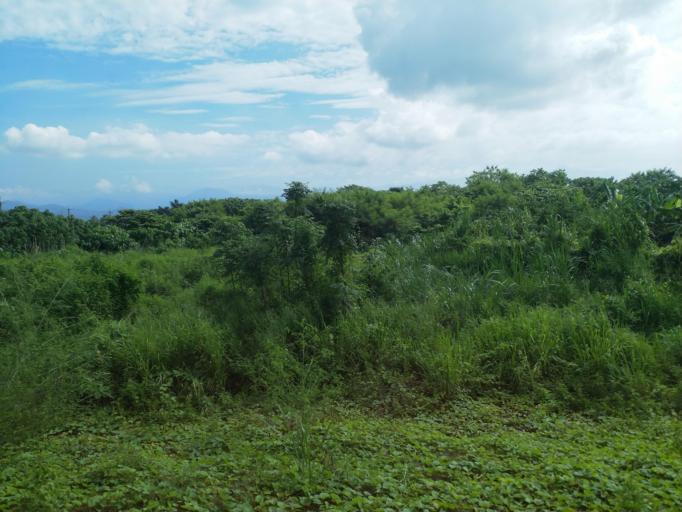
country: TW
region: Taiwan
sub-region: Pingtung
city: Pingtung
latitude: 22.8758
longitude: 120.4977
